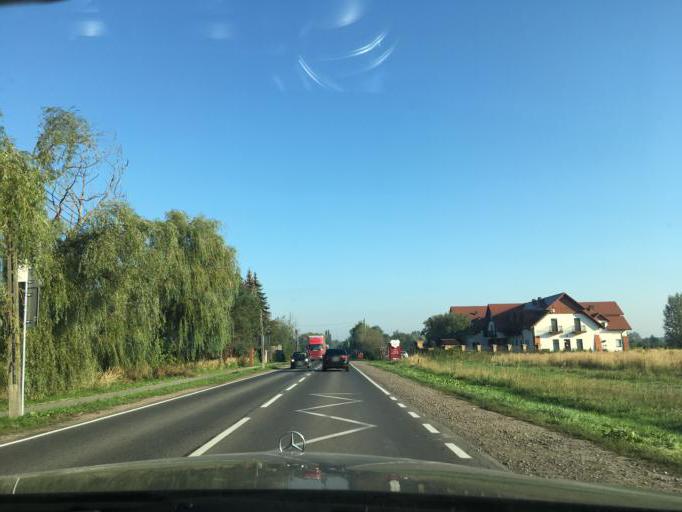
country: PL
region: Masovian Voivodeship
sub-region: Powiat grodziski
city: Grodzisk Mazowiecki
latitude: 52.1366
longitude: 20.6172
